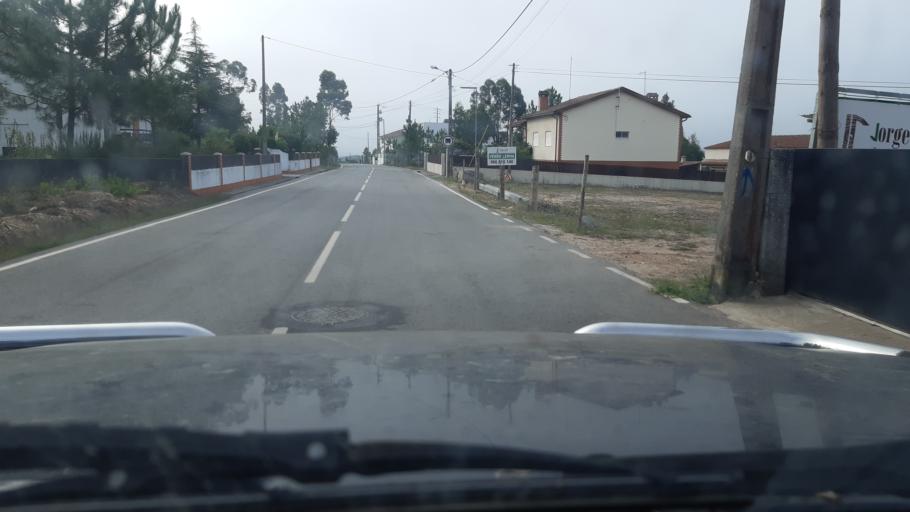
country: PT
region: Aveiro
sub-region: Agueda
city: Agueda
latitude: 40.5831
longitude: -8.4566
